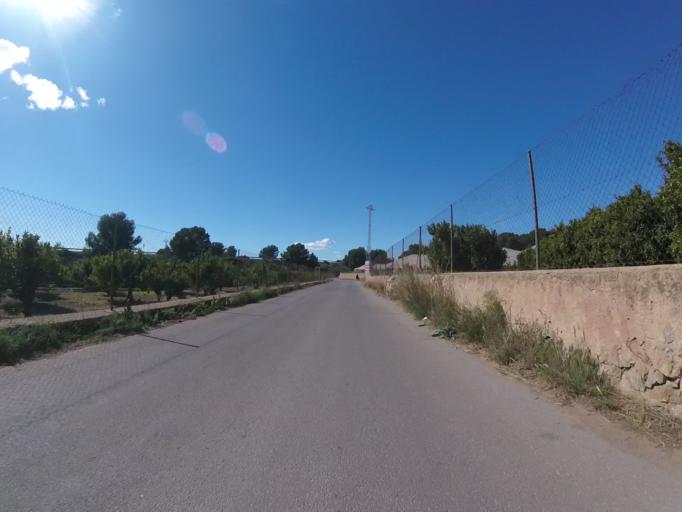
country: ES
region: Valencia
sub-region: Provincia de Castello
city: Benicassim
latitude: 40.0663
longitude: 0.0730
